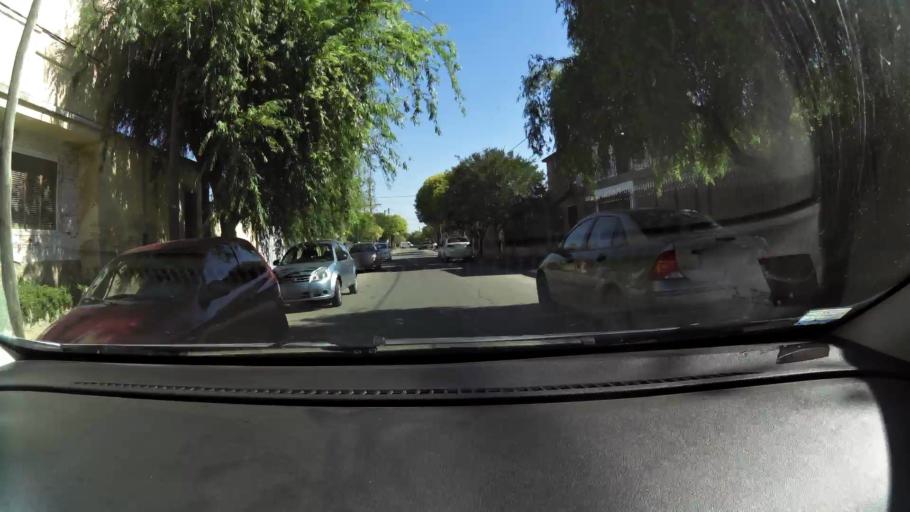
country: AR
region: Cordoba
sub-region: Departamento de Capital
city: Cordoba
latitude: -31.3701
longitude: -64.1818
